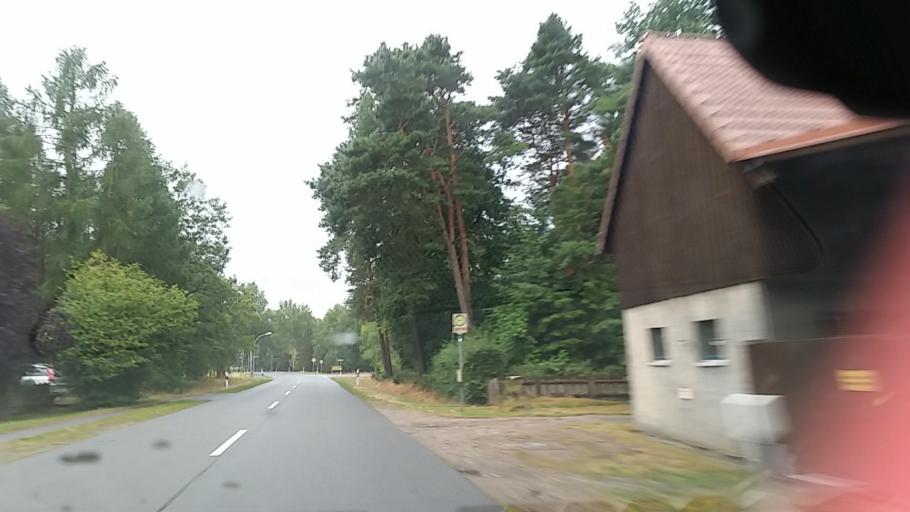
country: DE
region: Lower Saxony
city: Schoneworde
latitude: 52.6301
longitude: 10.6907
